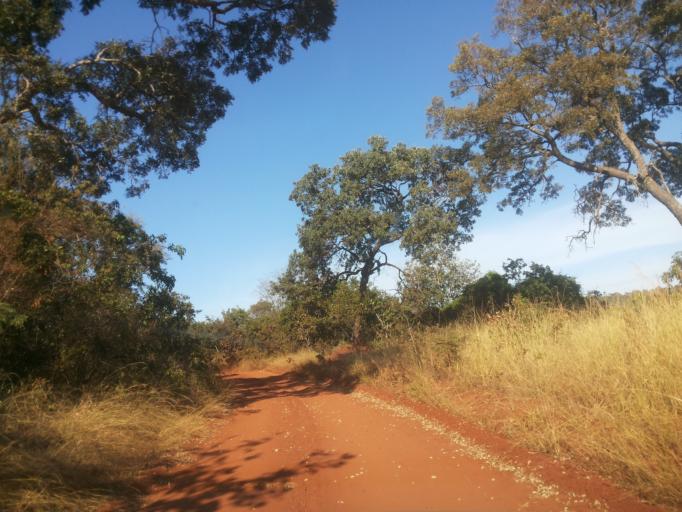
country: BR
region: Minas Gerais
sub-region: Ituiutaba
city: Ituiutaba
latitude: -19.0988
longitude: -49.4181
